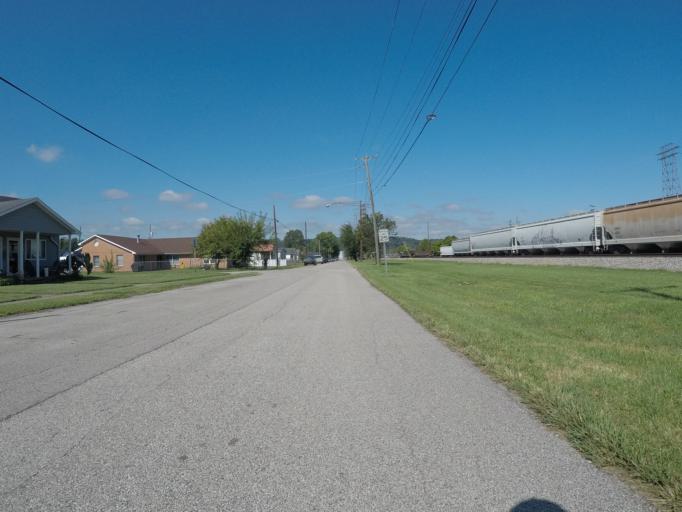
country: US
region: West Virginia
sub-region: Wayne County
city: Kenova
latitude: 38.4044
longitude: -82.5815
